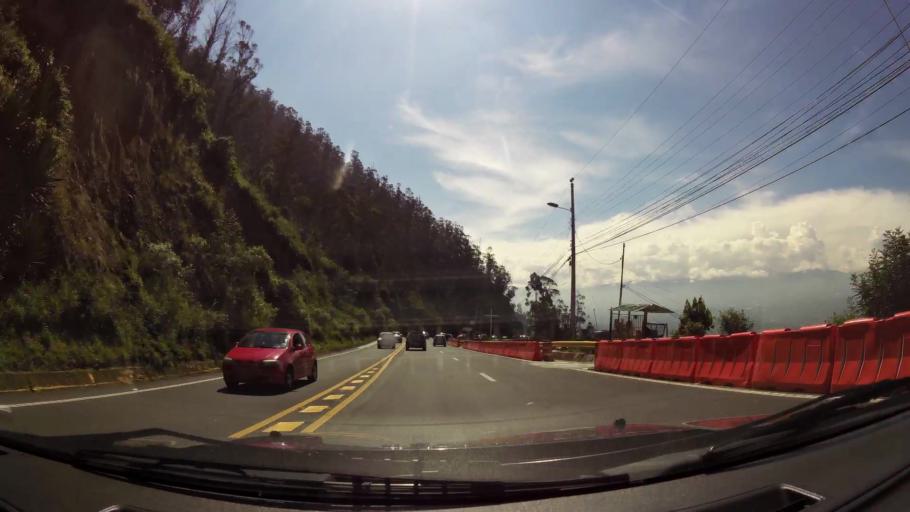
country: EC
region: Pichincha
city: Quito
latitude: -0.1935
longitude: -78.4646
